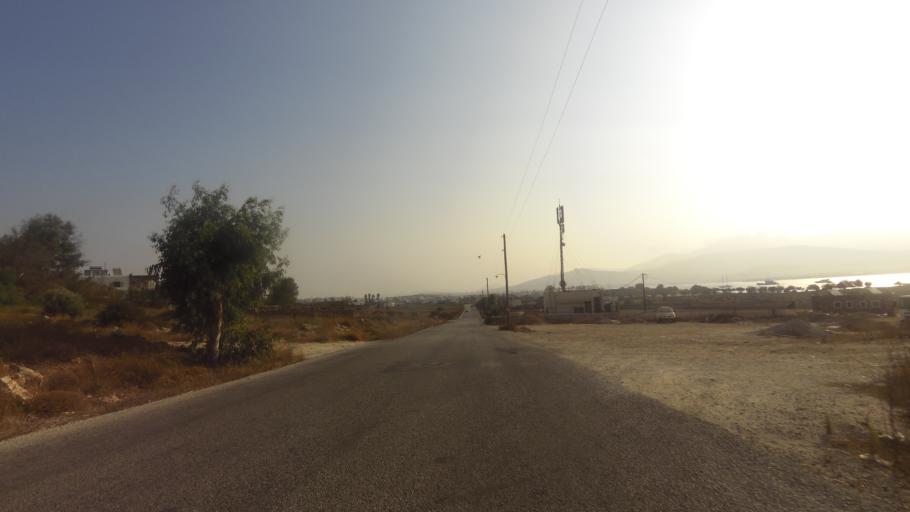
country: GR
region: South Aegean
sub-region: Nomos Kykladon
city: Antiparos
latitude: 37.0352
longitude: 25.0776
